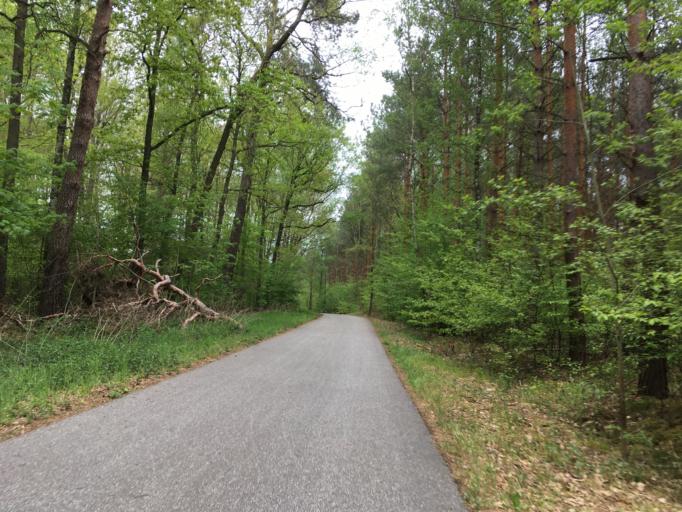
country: DE
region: Brandenburg
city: Bernau bei Berlin
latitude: 52.6913
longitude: 13.5398
